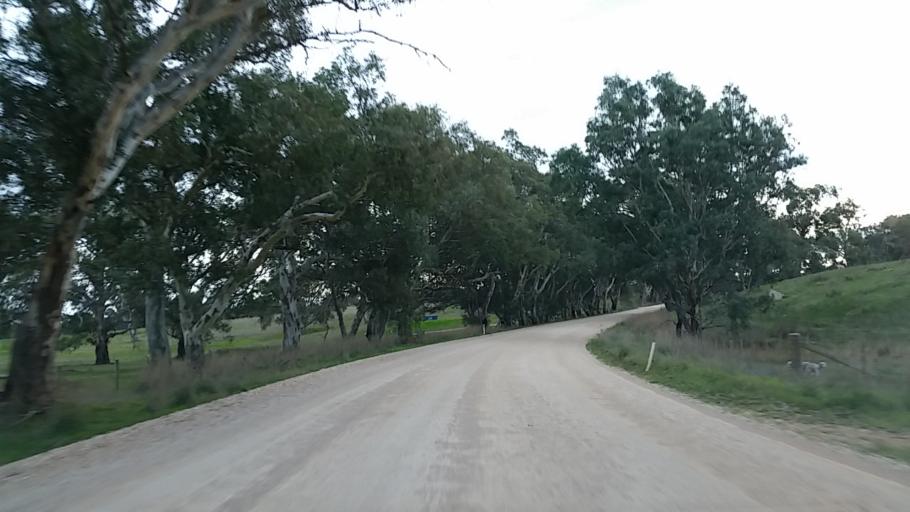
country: AU
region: South Australia
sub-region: Adelaide Hills
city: Birdwood
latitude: -34.8834
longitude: 139.0078
